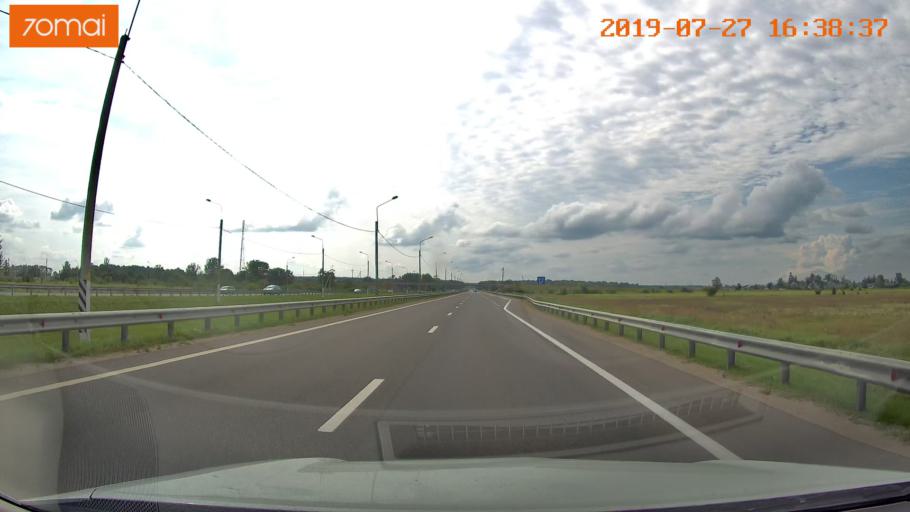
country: RU
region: Kaliningrad
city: Gvardeysk
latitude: 54.6490
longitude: 21.2233
